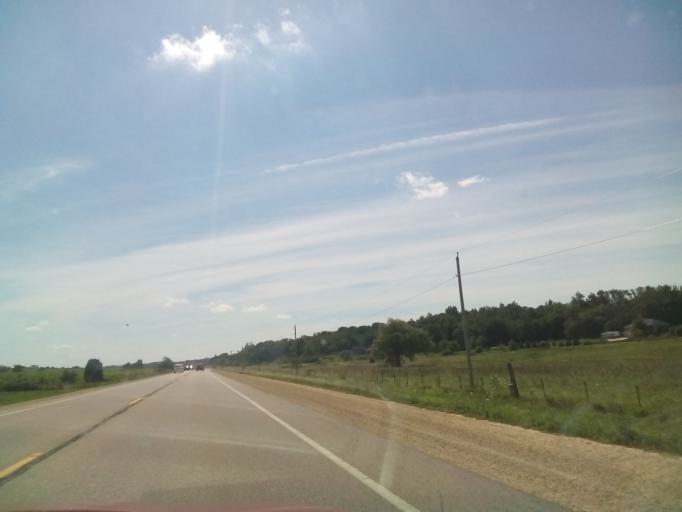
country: US
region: Wisconsin
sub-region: Green County
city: Monticello
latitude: 42.7659
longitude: -89.6215
